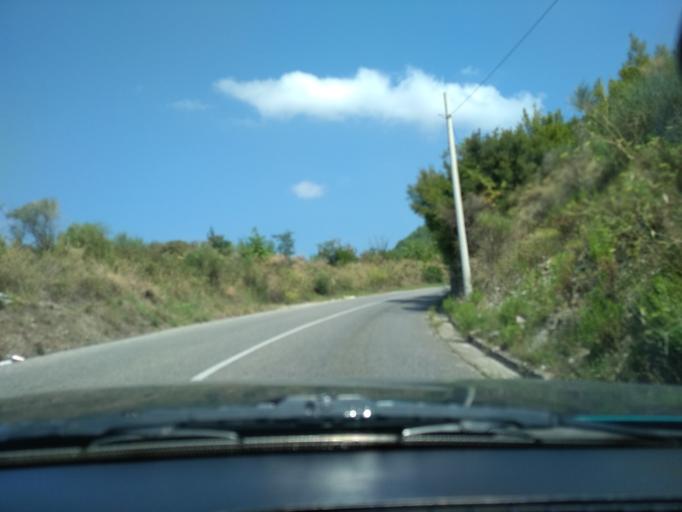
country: ME
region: Kotor
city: Kotor
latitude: 42.3873
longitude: 18.7572
